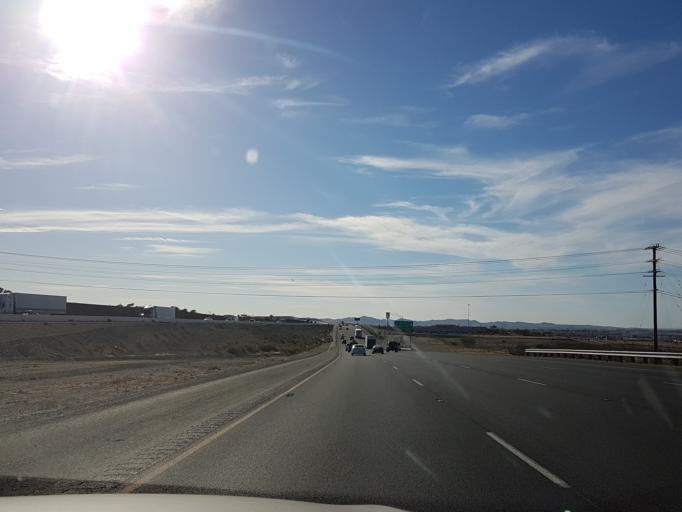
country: US
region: California
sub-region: San Bernardino County
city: Barstow Heights
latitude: 34.8861
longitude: -117.0486
